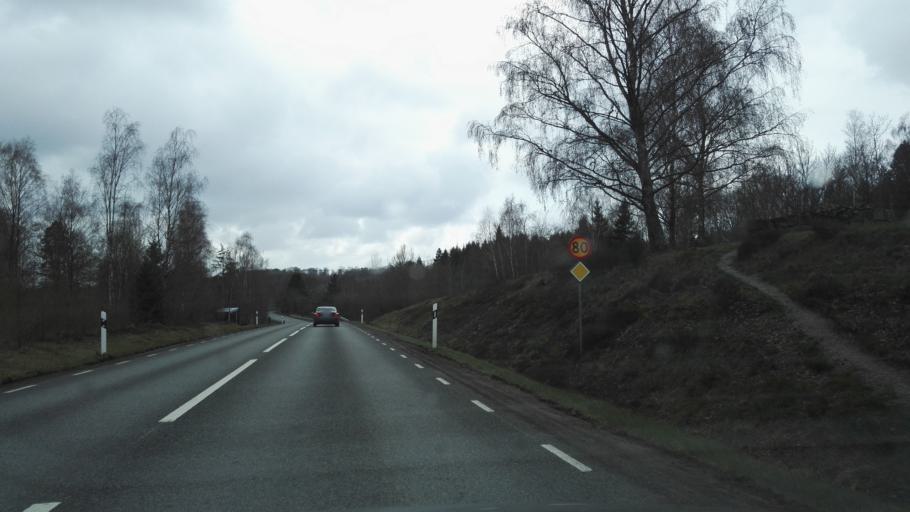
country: SE
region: Skane
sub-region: Hassleholms Kommun
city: Hastveda
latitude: 56.2093
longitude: 13.9415
